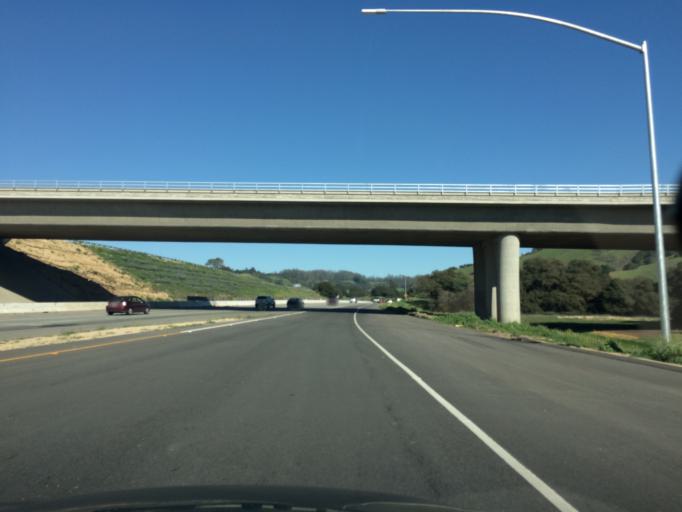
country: US
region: California
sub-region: San Benito County
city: Aromas
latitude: 36.8575
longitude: -121.6286
